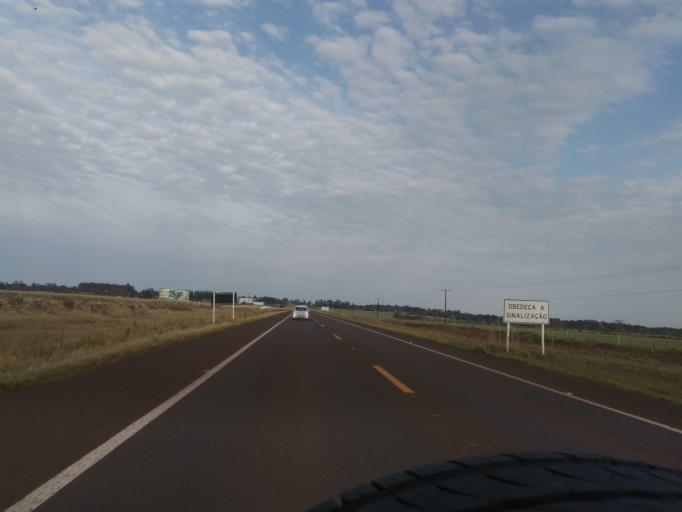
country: BR
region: Mato Grosso do Sul
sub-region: Ponta Pora
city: Ponta Pora
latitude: -22.6163
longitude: -55.6005
